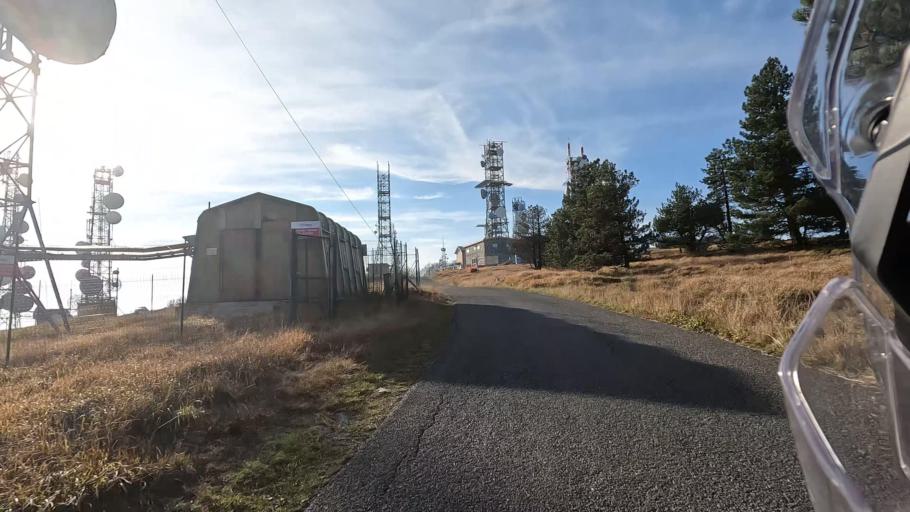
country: IT
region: Liguria
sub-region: Provincia di Genova
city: Sciarborasca
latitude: 44.4325
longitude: 8.5686
